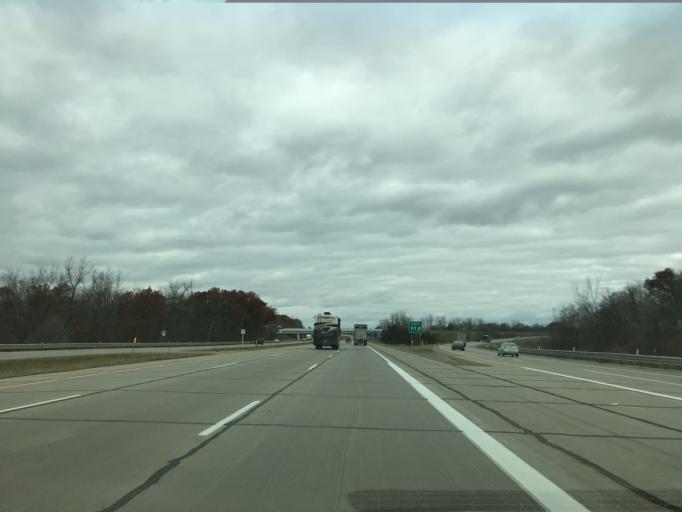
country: US
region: Michigan
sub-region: Eaton County
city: Waverly
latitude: 42.7752
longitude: -84.6695
